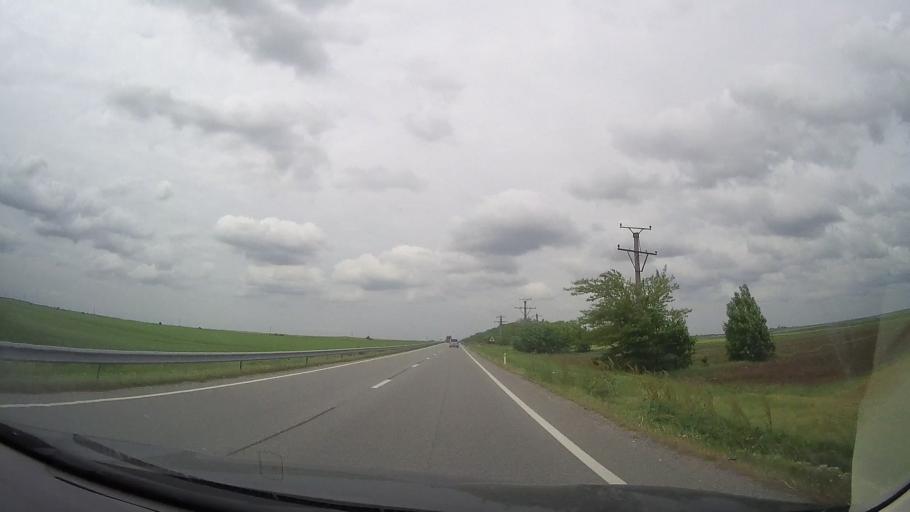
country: RO
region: Dolj
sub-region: Comuna Leu
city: Zanoaga
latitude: 44.1648
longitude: 24.0770
